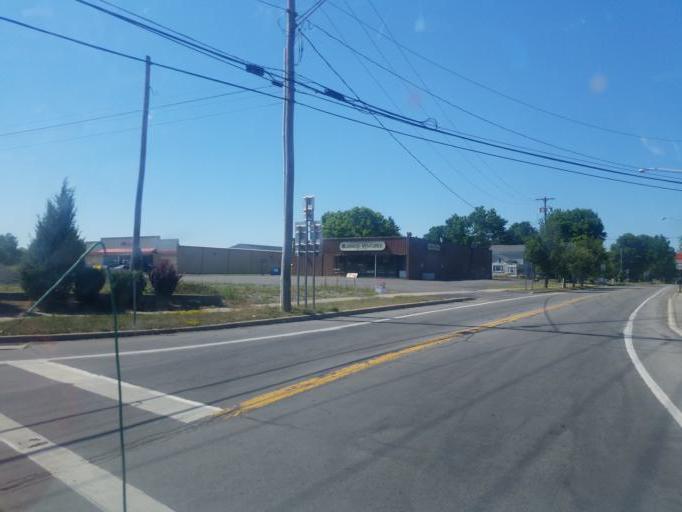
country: US
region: New York
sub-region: Ontario County
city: Phelps
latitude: 42.9626
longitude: -77.0754
